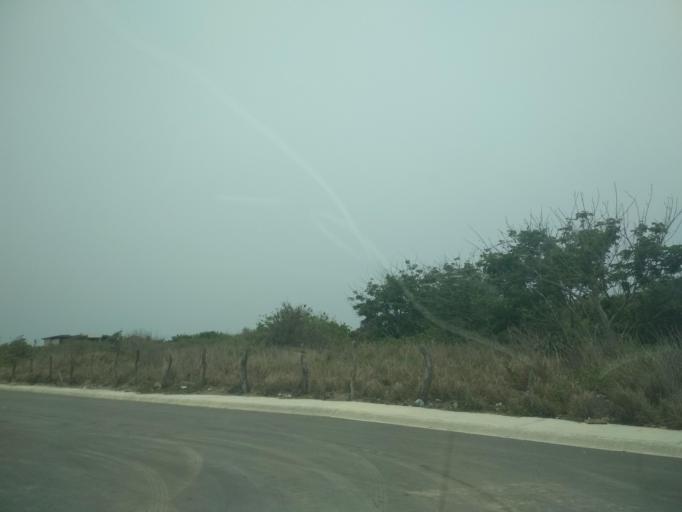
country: MX
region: Veracruz
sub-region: Alvarado
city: Playa de la Libertad
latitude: 19.0910
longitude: -96.0988
